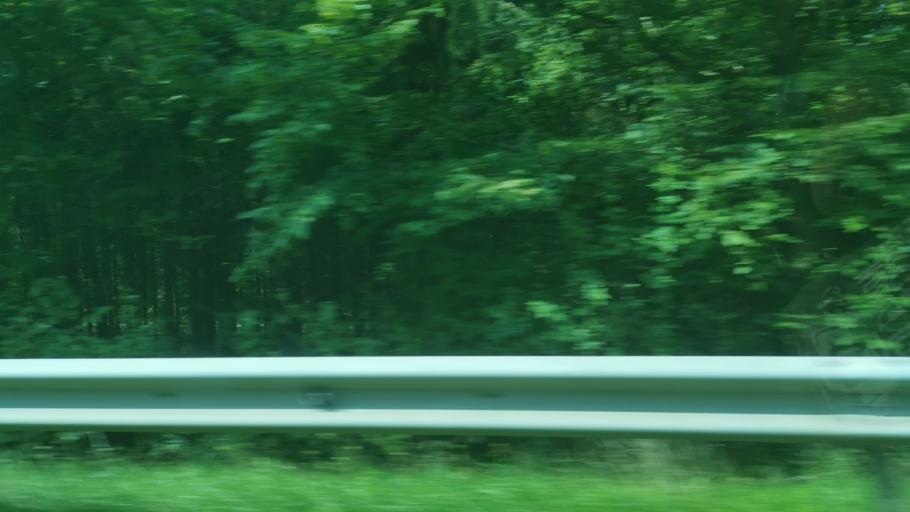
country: DE
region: Bavaria
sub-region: Upper Palatinate
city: Pemfling
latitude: 49.2782
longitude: 12.6258
